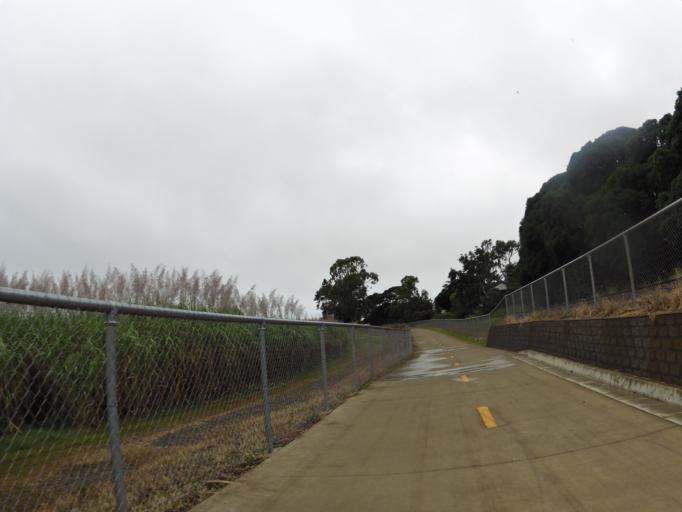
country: AU
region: Queensland
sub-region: Cairns
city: Redlynch
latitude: -16.8829
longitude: 145.7066
